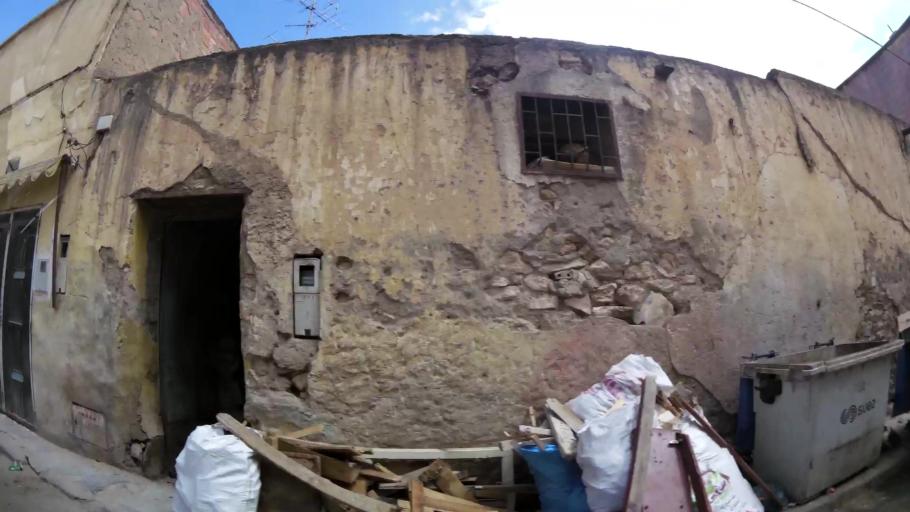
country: MA
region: Oriental
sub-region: Oujda-Angad
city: Oujda
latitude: 34.6806
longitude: -1.9008
